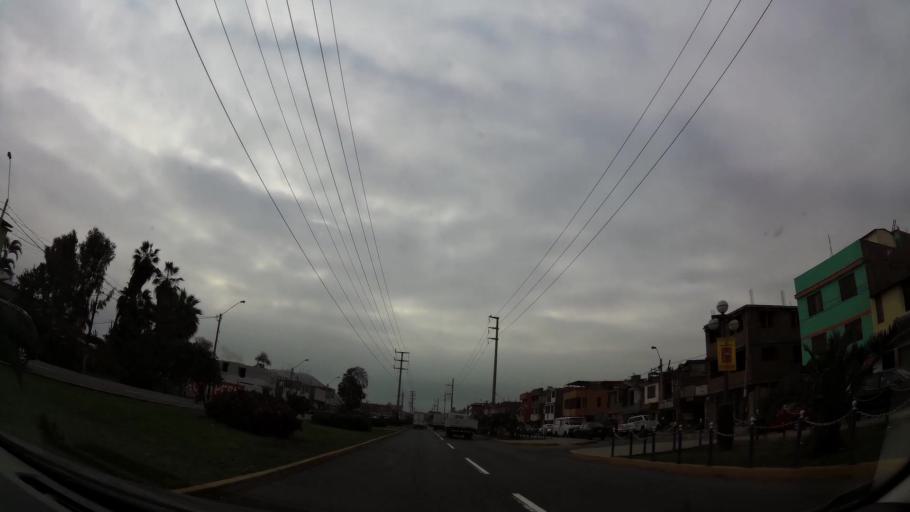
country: PE
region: Lima
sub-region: Lima
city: Surco
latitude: -12.1983
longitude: -76.9983
